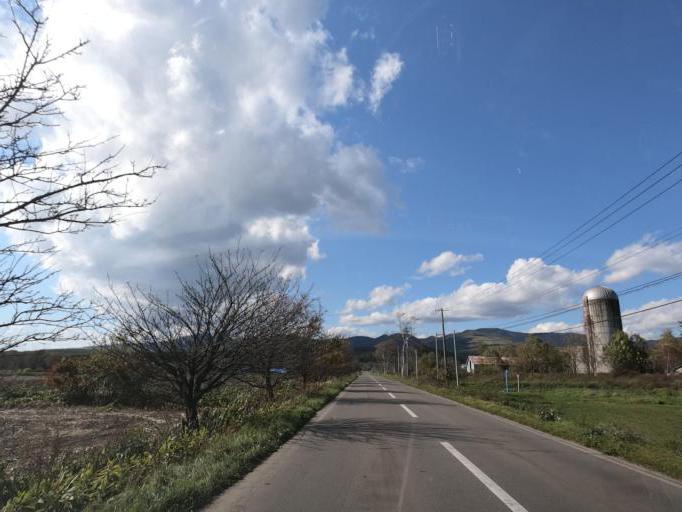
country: JP
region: Hokkaido
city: Otofuke
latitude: 43.2578
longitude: 143.2516
